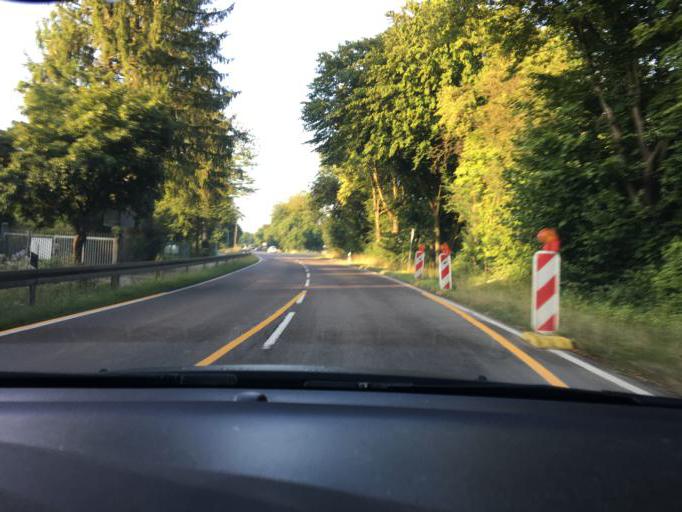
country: DE
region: Bavaria
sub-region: Upper Bavaria
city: Erding
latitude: 48.3006
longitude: 11.9155
